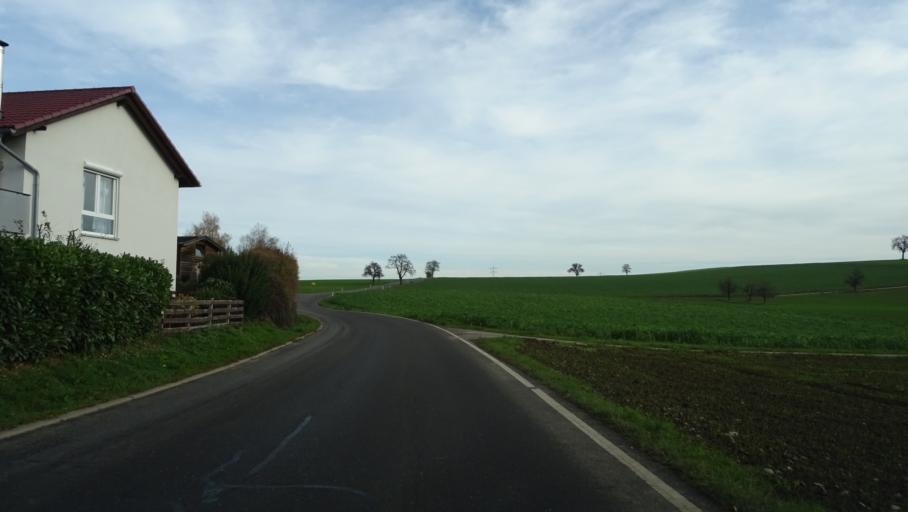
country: DE
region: Baden-Wuerttemberg
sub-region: Karlsruhe Region
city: Neckargerach
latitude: 49.3949
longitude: 9.1000
